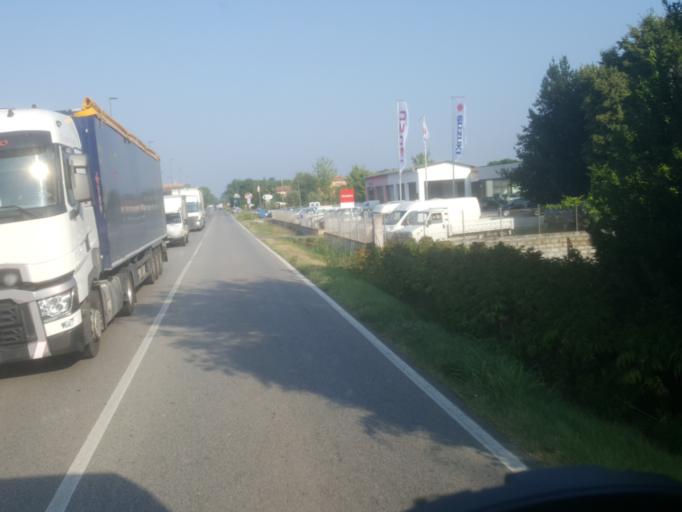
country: IT
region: Emilia-Romagna
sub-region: Provincia di Ravenna
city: Mezzano
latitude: 44.4583
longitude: 12.1015
